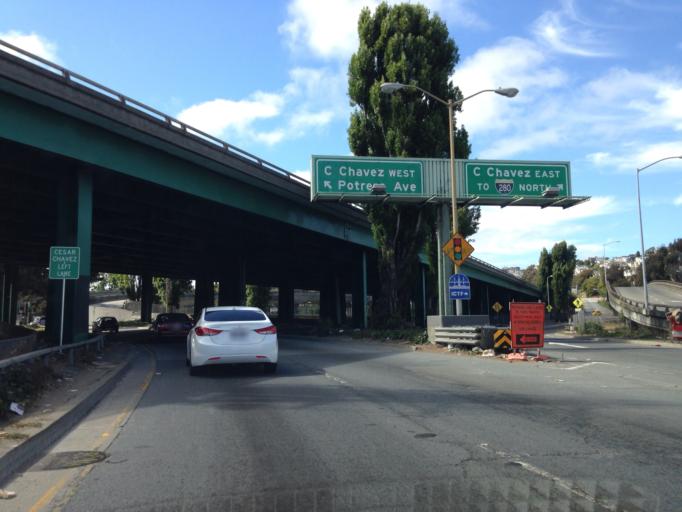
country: US
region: California
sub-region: San Francisco County
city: San Francisco
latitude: 37.7481
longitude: -122.4037
